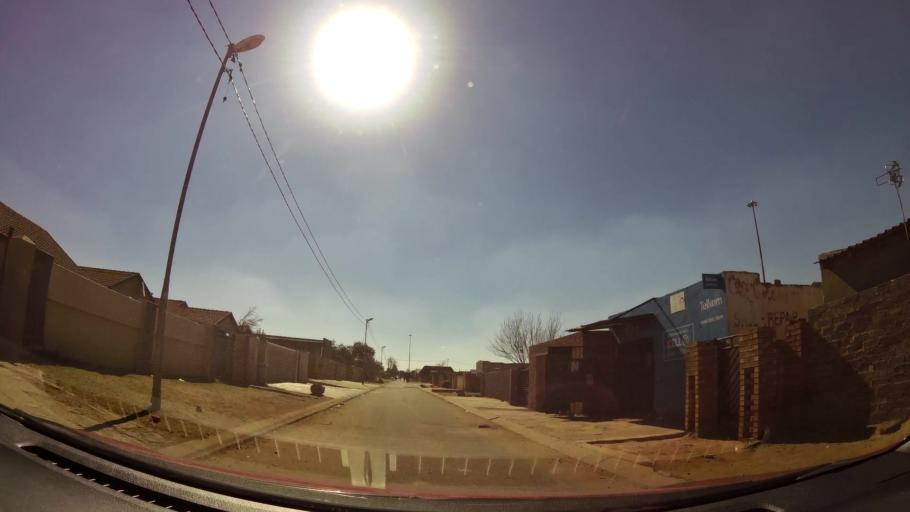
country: ZA
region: Gauteng
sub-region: City of Johannesburg Metropolitan Municipality
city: Soweto
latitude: -26.2469
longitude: 27.8059
